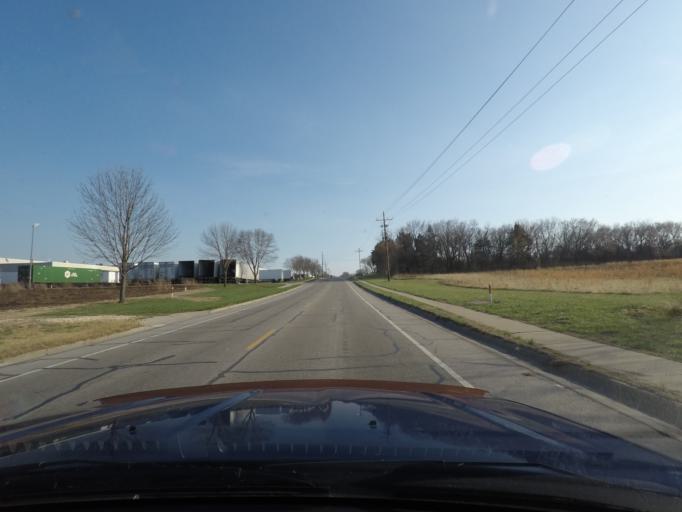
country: US
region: Kansas
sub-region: Douglas County
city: Lawrence
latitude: 38.9876
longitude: -95.2605
